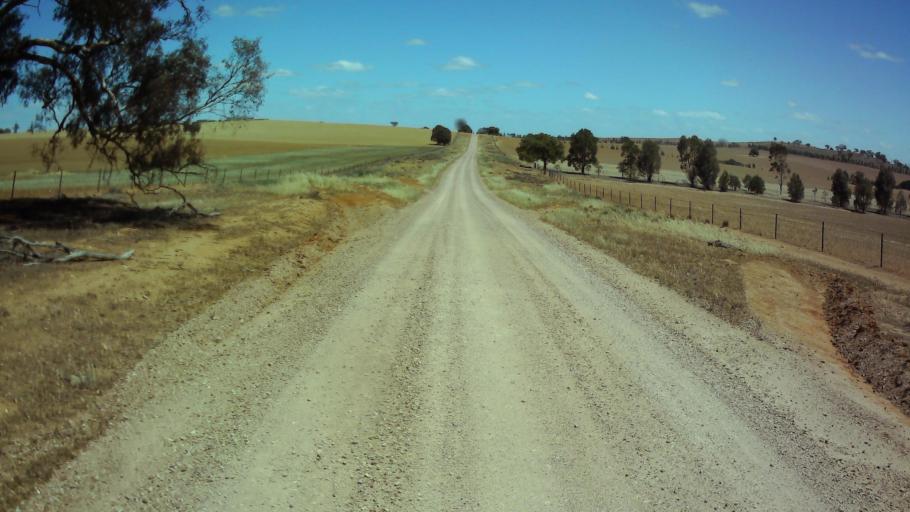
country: AU
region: New South Wales
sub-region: Weddin
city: Grenfell
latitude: -33.9428
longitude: 148.3298
